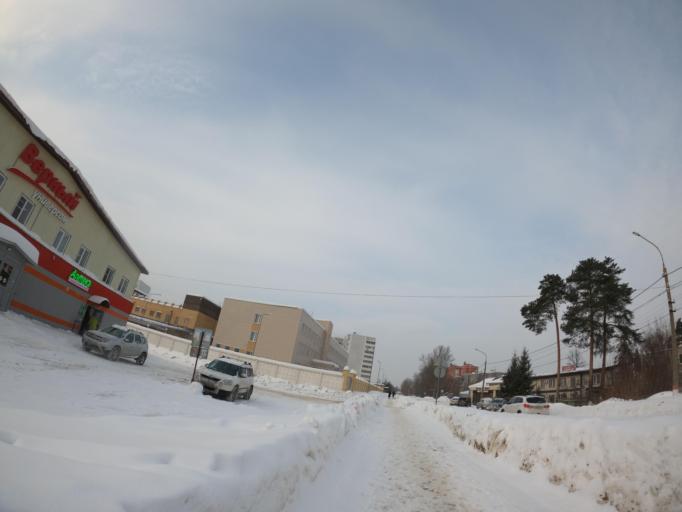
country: RU
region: Moskovskaya
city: Elektrogorsk
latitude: 55.8866
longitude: 38.7781
